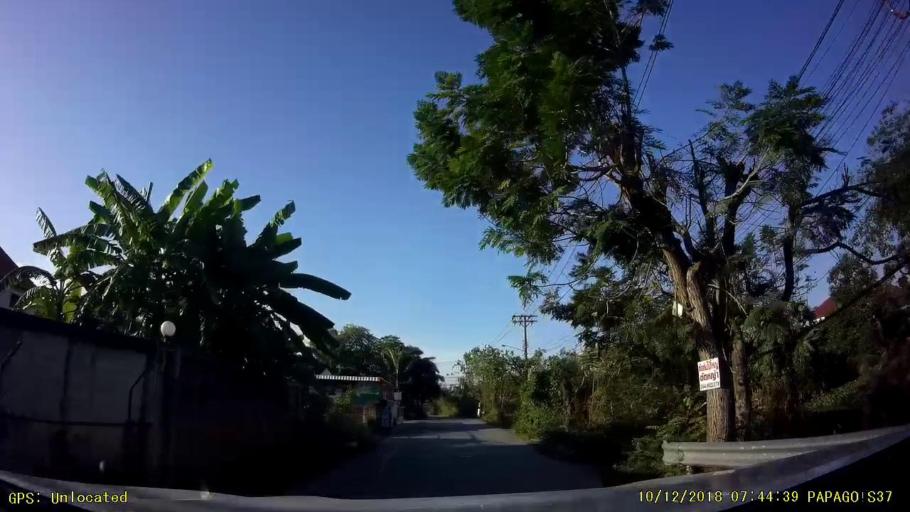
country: TH
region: Bangkok
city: Lat Krabang
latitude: 13.7878
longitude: 100.8233
